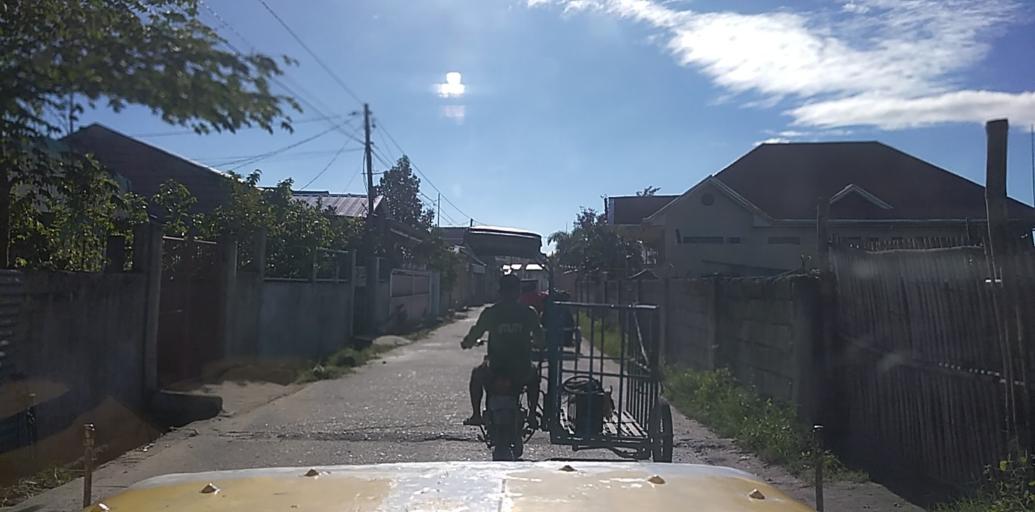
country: PH
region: Central Luzon
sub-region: Province of Pampanga
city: San Patricio
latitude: 15.1174
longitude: 120.7074
